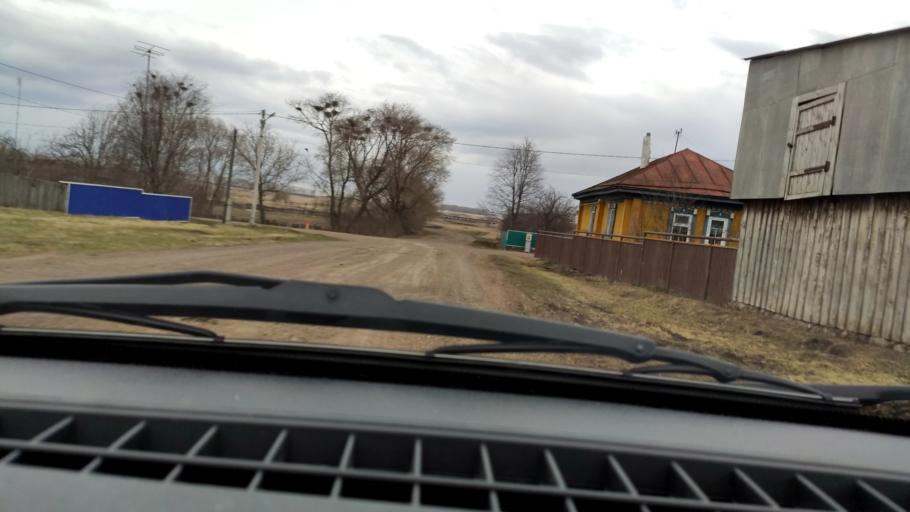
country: RU
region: Bashkortostan
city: Semiletka
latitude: 55.2902
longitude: 54.7018
